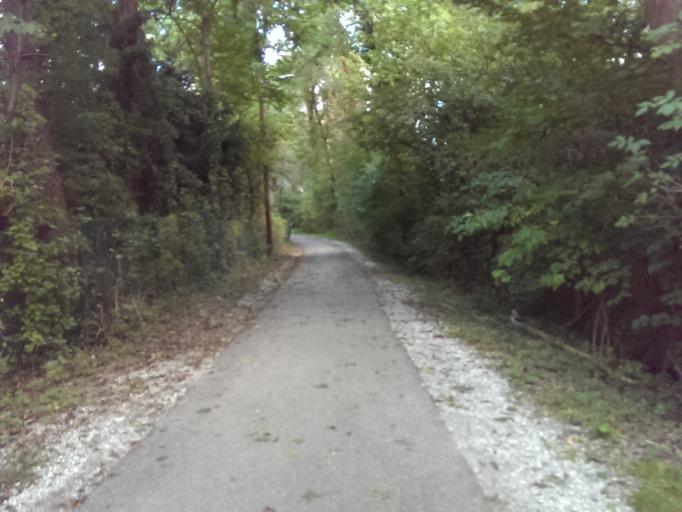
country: AT
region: Styria
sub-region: Graz Stadt
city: Graz
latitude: 47.0610
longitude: 15.4792
